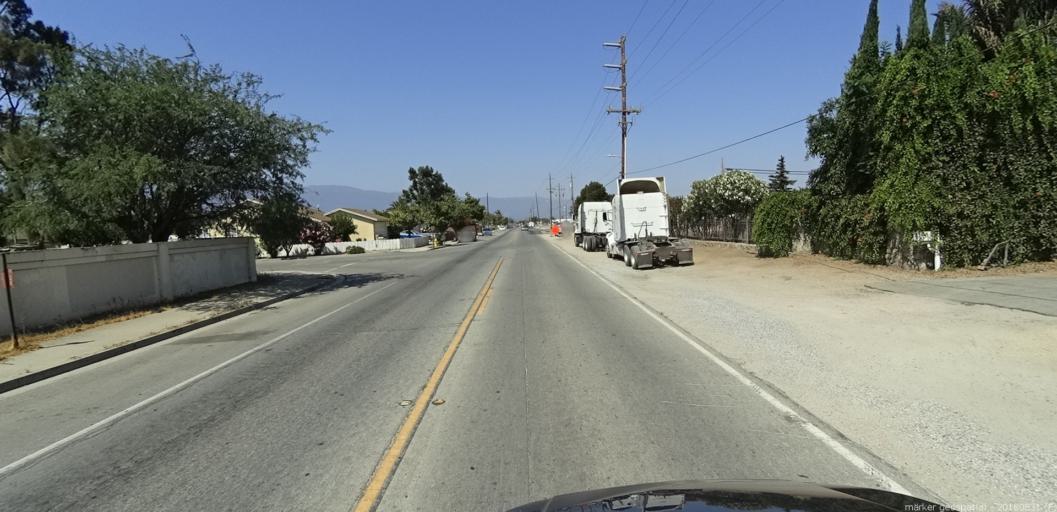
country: US
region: California
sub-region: Monterey County
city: Soledad
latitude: 36.4259
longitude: -121.3113
